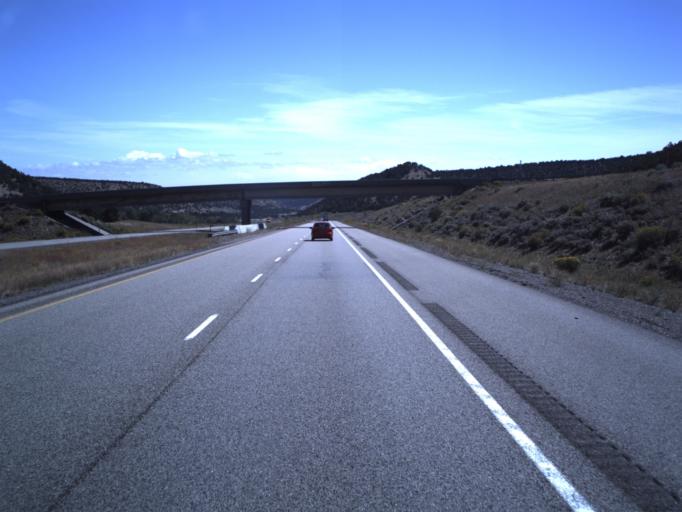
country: US
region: Utah
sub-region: Wayne County
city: Loa
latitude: 38.7569
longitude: -111.4272
